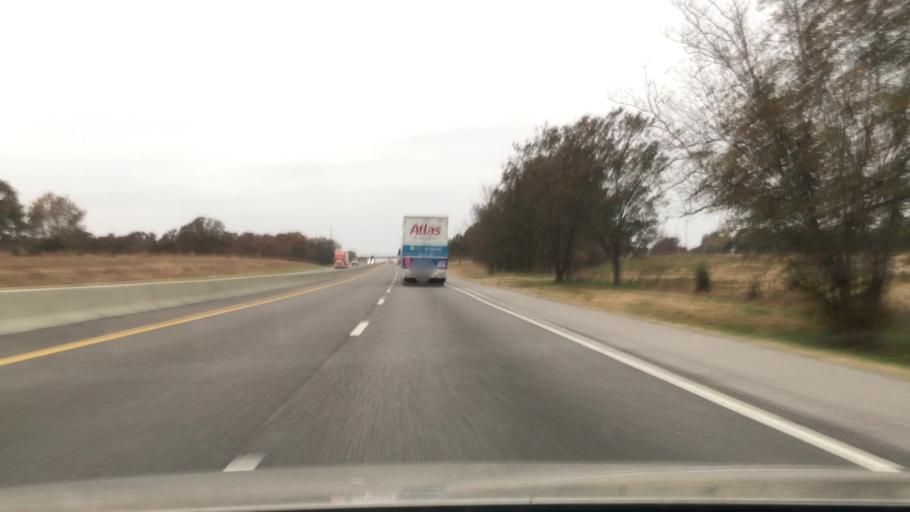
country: US
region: Oklahoma
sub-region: Lincoln County
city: Chandler
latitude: 35.7240
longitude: -96.8596
